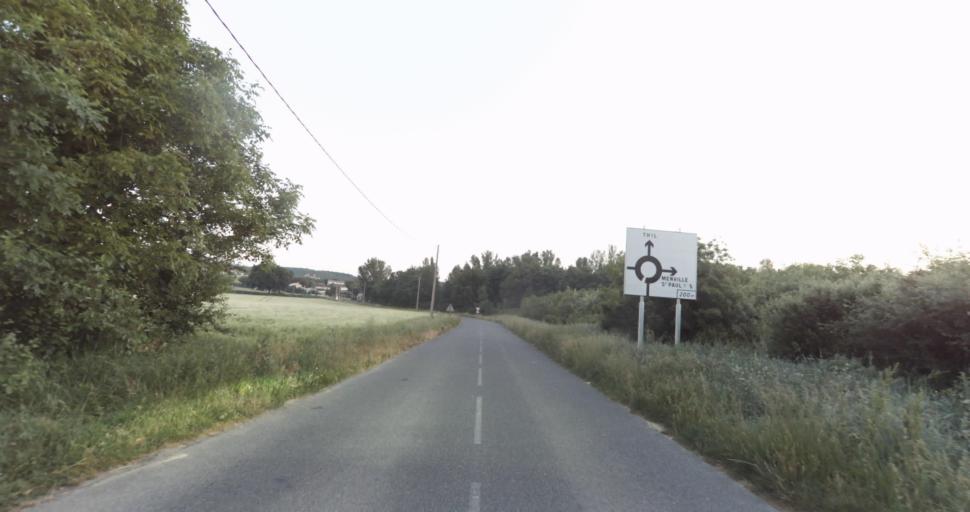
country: FR
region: Midi-Pyrenees
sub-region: Departement de la Haute-Garonne
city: Levignac
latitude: 43.6715
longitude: 1.1890
